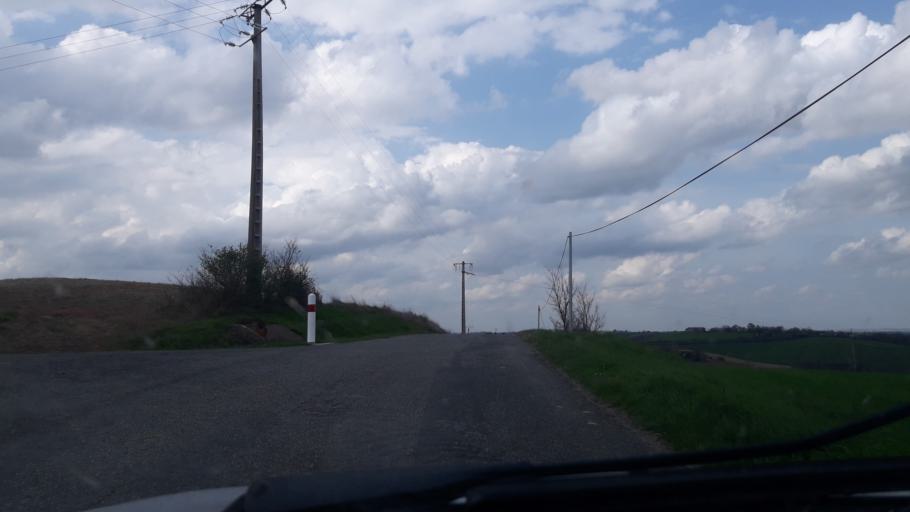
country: FR
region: Midi-Pyrenees
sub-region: Departement de la Haute-Garonne
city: Montesquieu-Volvestre
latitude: 43.2030
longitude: 1.3090
